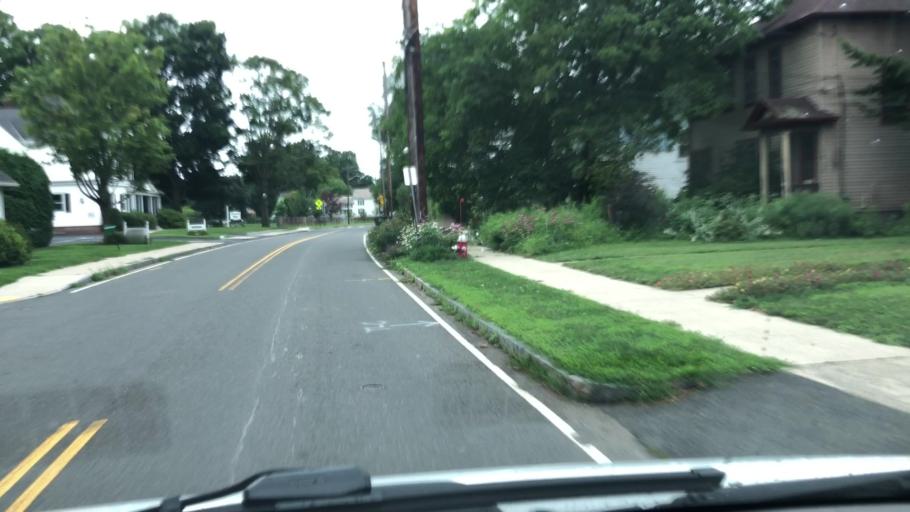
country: US
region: Massachusetts
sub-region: Hampshire County
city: Northampton
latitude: 42.3290
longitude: -72.6278
